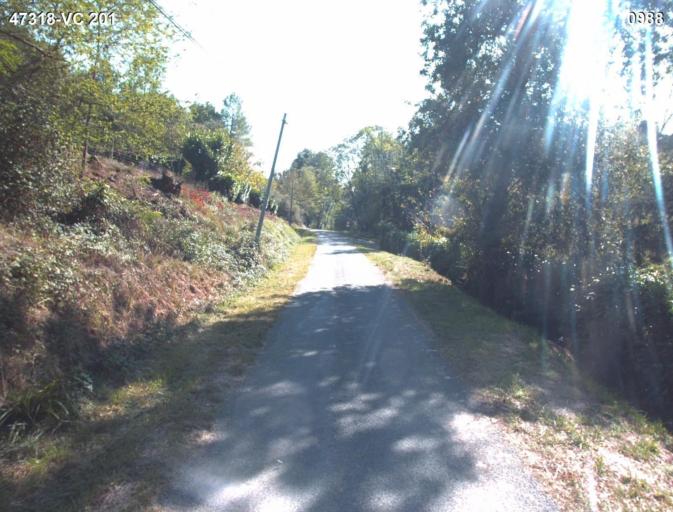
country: FR
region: Aquitaine
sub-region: Departement du Lot-et-Garonne
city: Vianne
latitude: 44.2059
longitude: 0.3164
